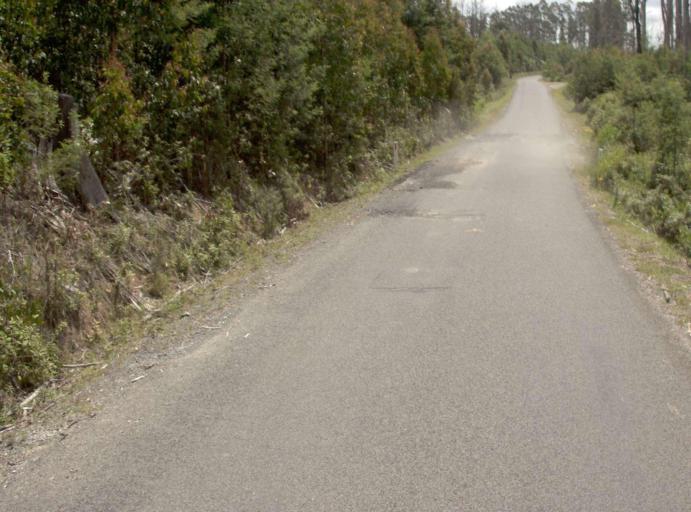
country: AU
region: Victoria
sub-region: Latrobe
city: Traralgon
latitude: -38.4309
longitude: 146.5449
